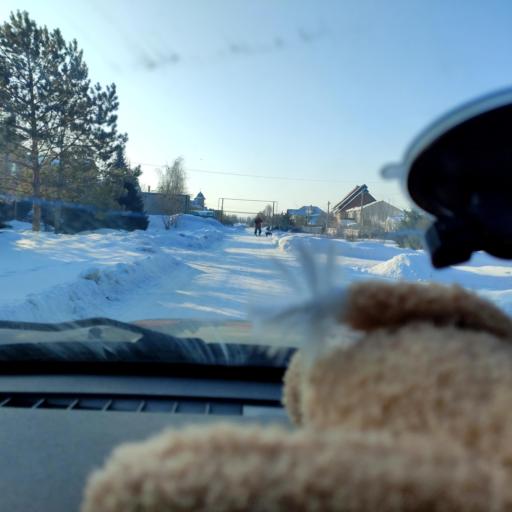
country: RU
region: Samara
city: Podstepki
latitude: 53.5181
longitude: 49.1663
